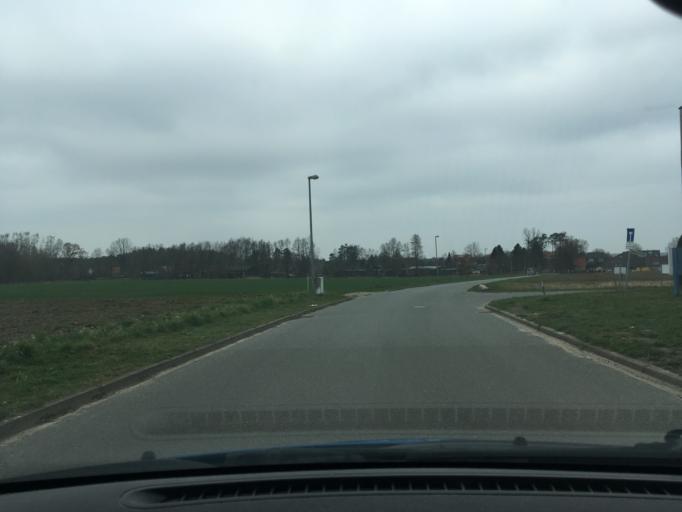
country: DE
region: Lower Saxony
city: Kirchgellersen
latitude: 53.2268
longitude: 10.2845
